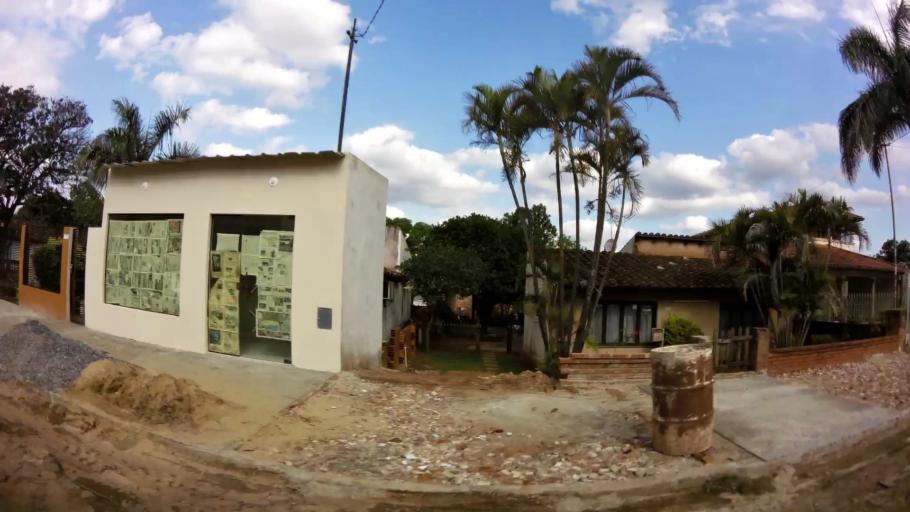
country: PY
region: Central
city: Fernando de la Mora
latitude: -25.3476
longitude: -57.5438
